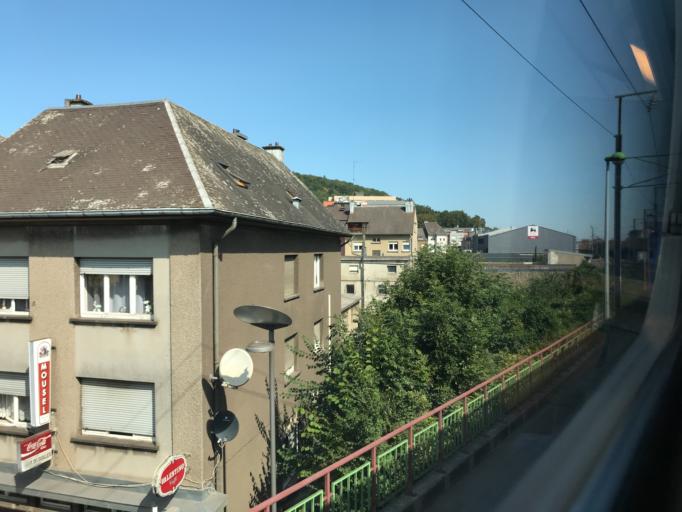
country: LU
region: Luxembourg
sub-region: Canton d'Esch-sur-Alzette
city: Differdange
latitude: 49.5226
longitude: 5.8919
